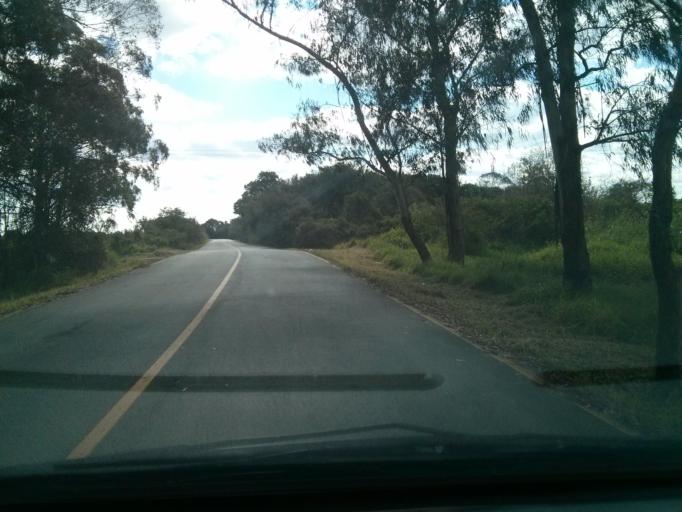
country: BR
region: Parana
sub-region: Sao Jose Dos Pinhais
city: Sao Jose dos Pinhais
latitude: -25.5371
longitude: -49.2258
